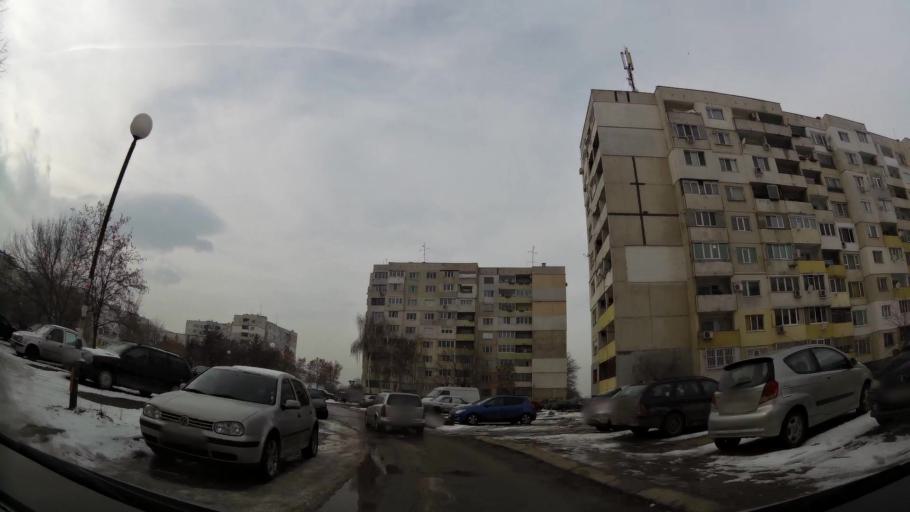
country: BG
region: Sofia-Capital
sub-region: Stolichna Obshtina
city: Sofia
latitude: 42.7146
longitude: 23.3770
